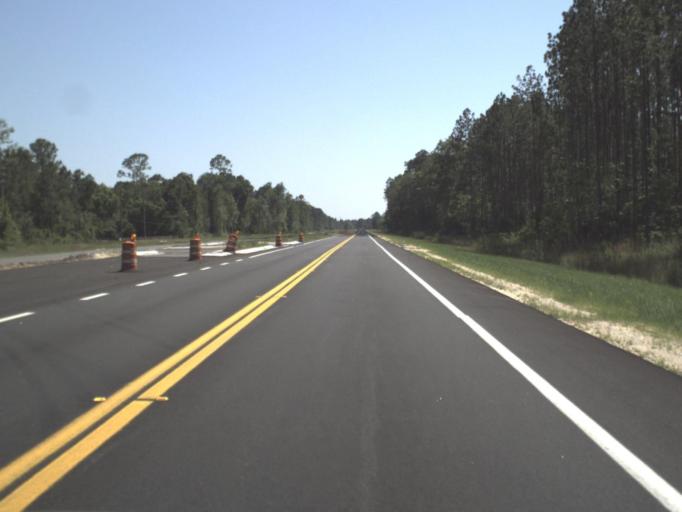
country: US
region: Florida
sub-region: Duval County
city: Baldwin
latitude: 30.3536
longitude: -81.9506
